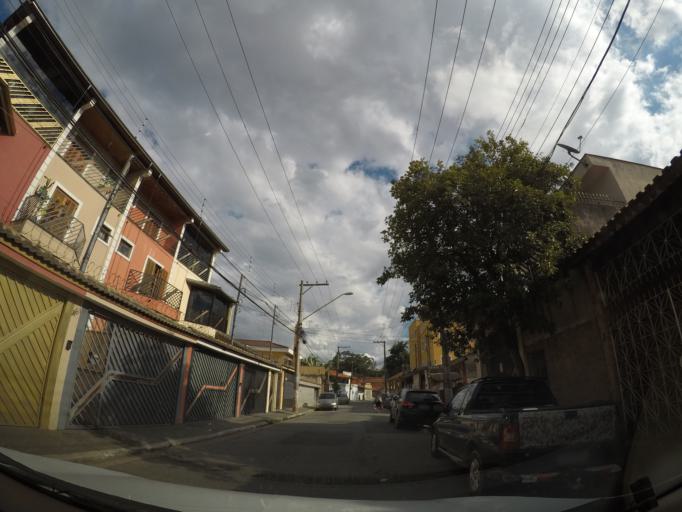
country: BR
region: Sao Paulo
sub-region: Guarulhos
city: Guarulhos
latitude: -23.4766
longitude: -46.5527
